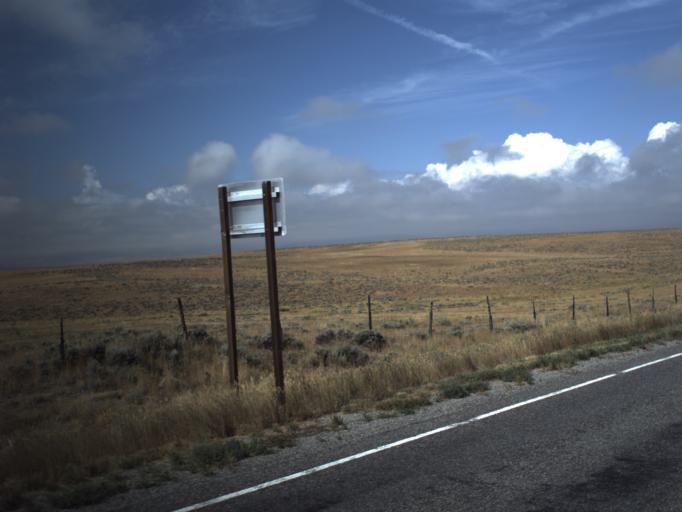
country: US
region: Wyoming
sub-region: Uinta County
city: Evanston
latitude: 41.4390
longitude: -111.0711
